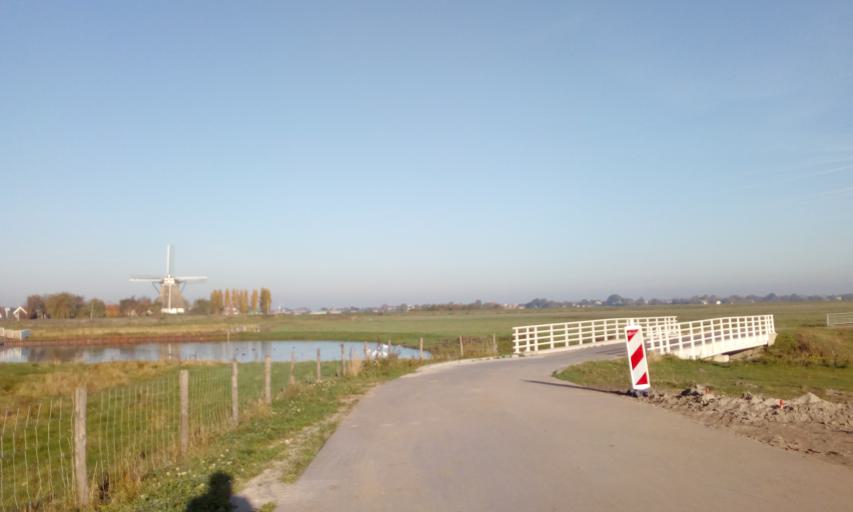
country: NL
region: South Holland
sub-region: Gemeente Pijnacker-Nootdorp
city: Pijnacker
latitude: 51.9778
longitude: 4.4316
